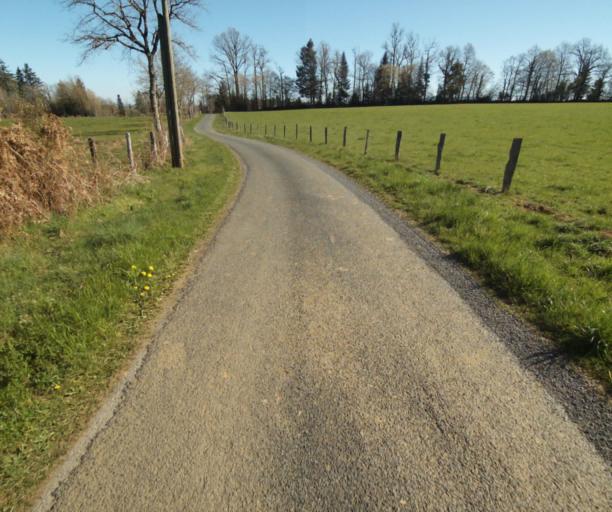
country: FR
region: Limousin
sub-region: Departement de la Correze
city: Chamboulive
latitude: 45.4119
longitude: 1.6876
